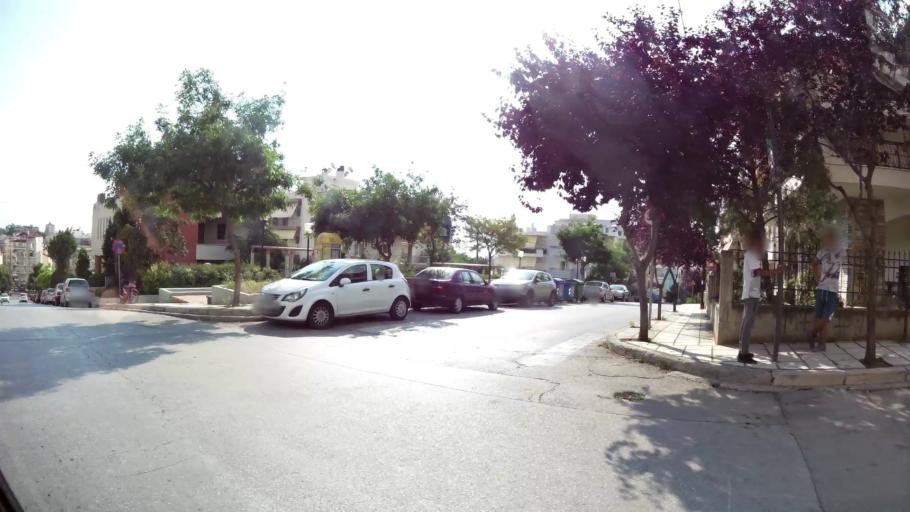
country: GR
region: Central Macedonia
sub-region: Nomos Thessalonikis
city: Polichni
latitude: 40.6601
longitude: 22.9560
